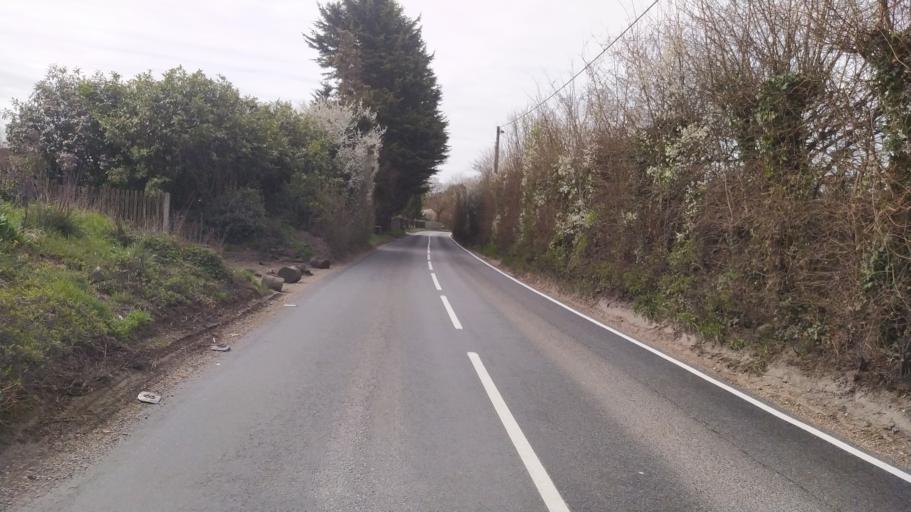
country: GB
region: England
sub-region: Hampshire
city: Fareham
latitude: 50.8651
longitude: -1.2291
